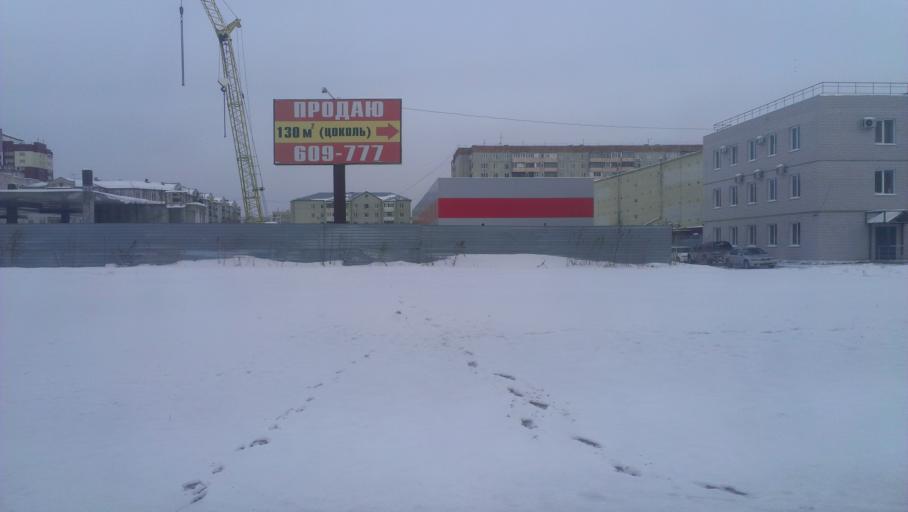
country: RU
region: Altai Krai
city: Novosilikatnyy
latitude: 53.3294
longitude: 83.6722
